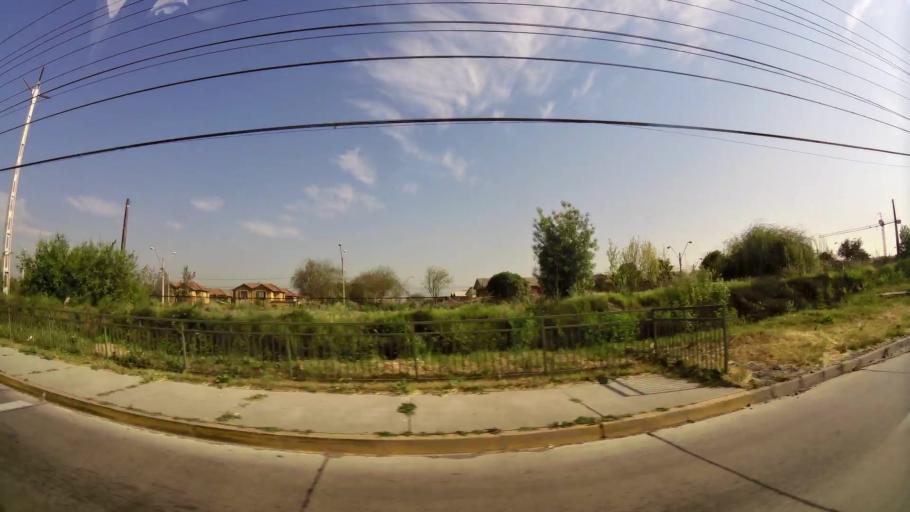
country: CL
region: Santiago Metropolitan
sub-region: Provincia de Maipo
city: San Bernardo
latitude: -33.5446
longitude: -70.7823
